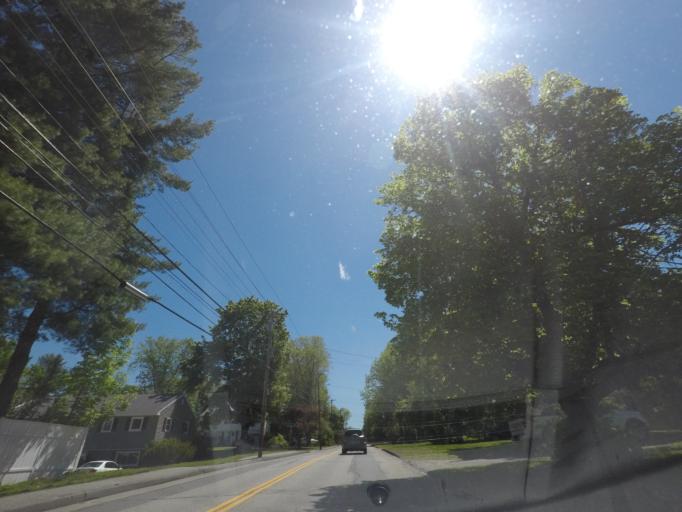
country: US
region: Maine
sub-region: Kennebec County
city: Augusta
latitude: 44.3195
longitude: -69.8098
